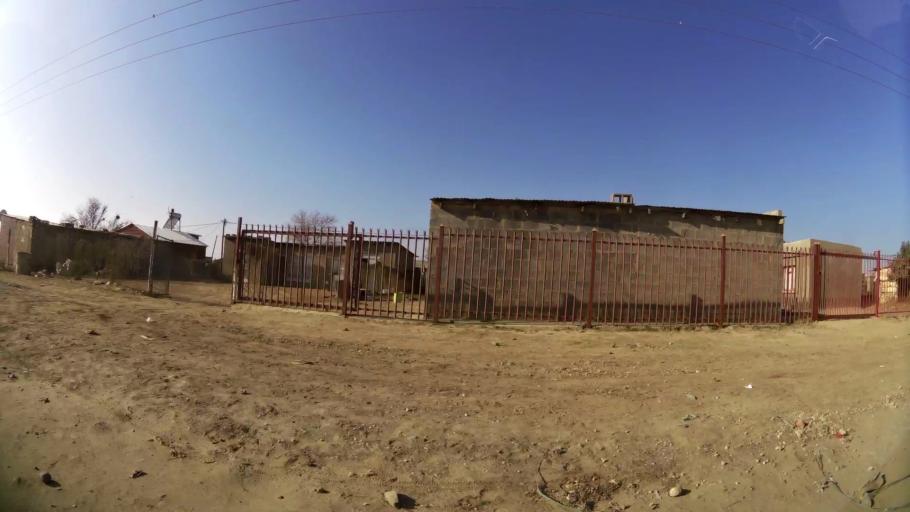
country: ZA
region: Orange Free State
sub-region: Mangaung Metropolitan Municipality
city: Bloemfontein
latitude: -29.1979
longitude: 26.2614
